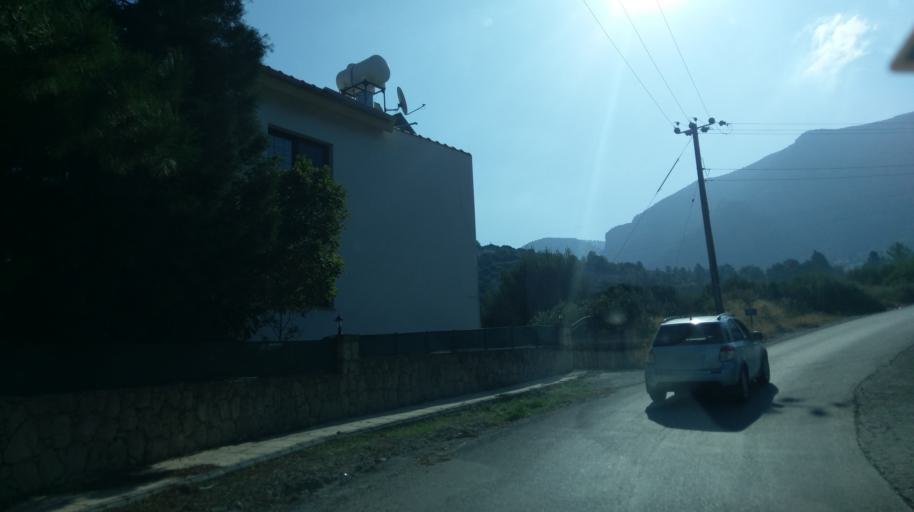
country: CY
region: Keryneia
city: Kyrenia
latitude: 35.3277
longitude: 33.2578
